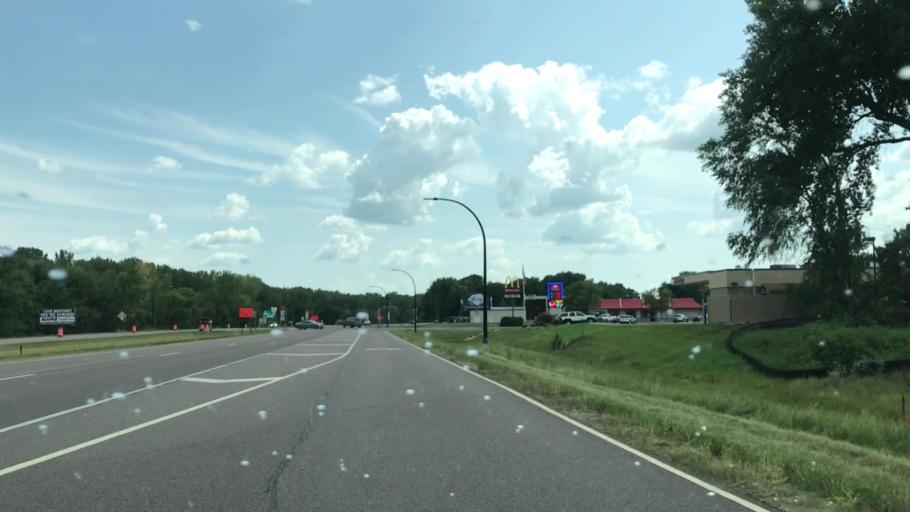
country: US
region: Minnesota
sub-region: Nicollet County
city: Saint Peter
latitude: 44.3412
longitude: -93.9491
